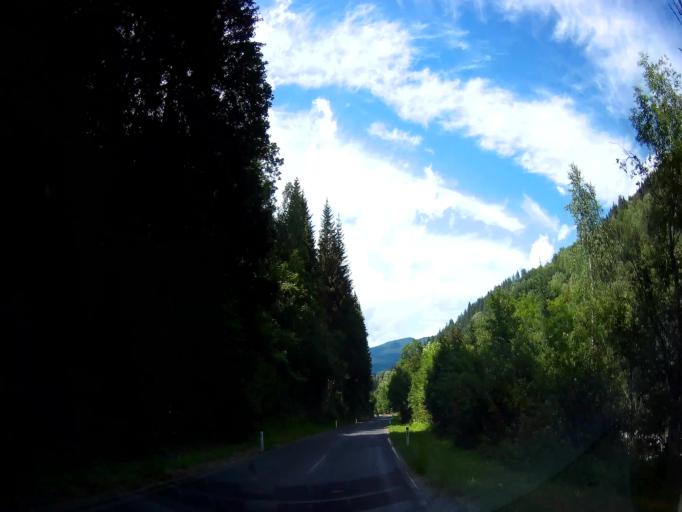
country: AT
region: Styria
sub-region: Politischer Bezirk Murau
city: Stadl an der Mur
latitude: 47.0531
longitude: 13.9962
